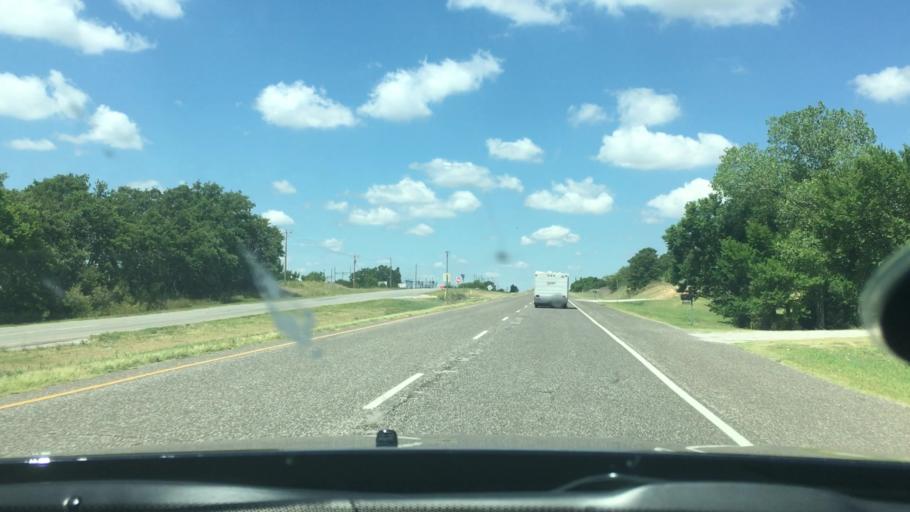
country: US
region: Oklahoma
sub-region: Carter County
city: Lone Grove
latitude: 34.1730
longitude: -97.3248
